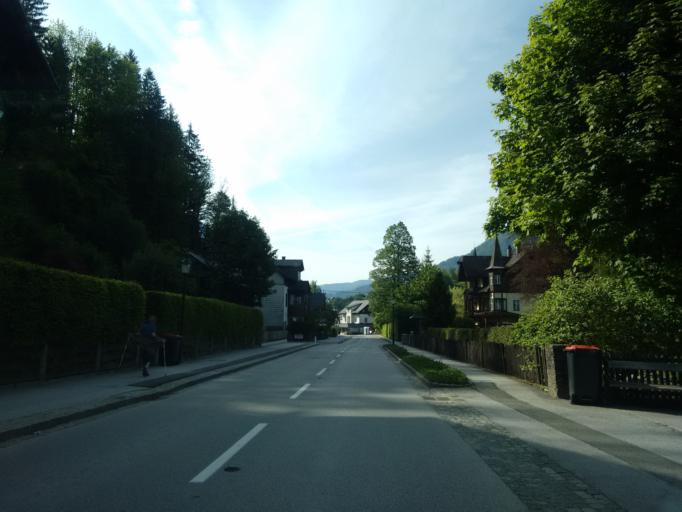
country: AT
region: Styria
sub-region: Politischer Bezirk Liezen
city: Bad Aussee
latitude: 47.6141
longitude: 13.7762
